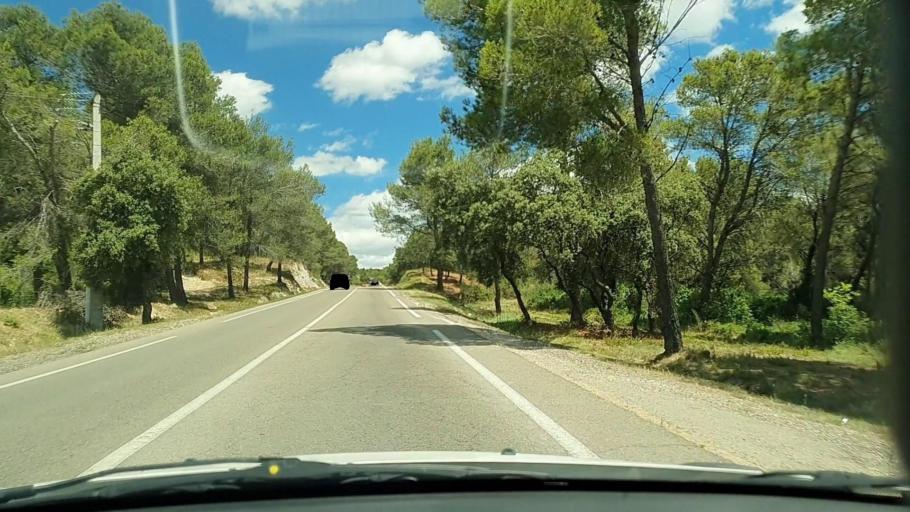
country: FR
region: Languedoc-Roussillon
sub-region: Departement du Gard
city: Poulx
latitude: 43.8929
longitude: 4.4195
